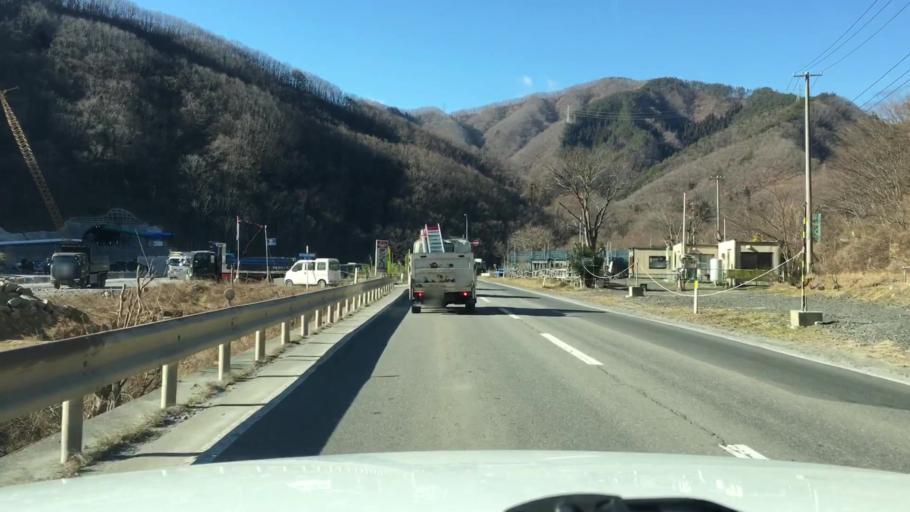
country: JP
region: Iwate
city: Miyako
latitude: 39.6234
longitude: 141.8252
